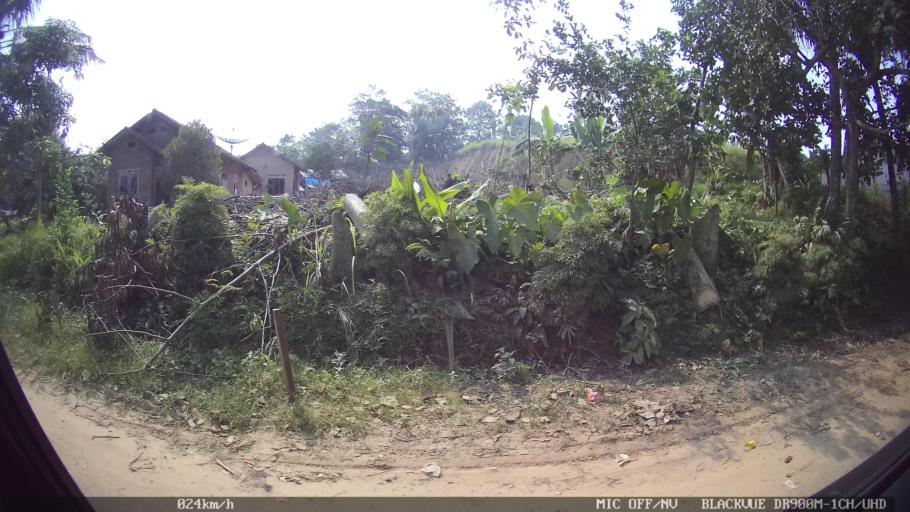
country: ID
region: Lampung
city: Pringsewu
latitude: -5.3923
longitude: 104.9933
